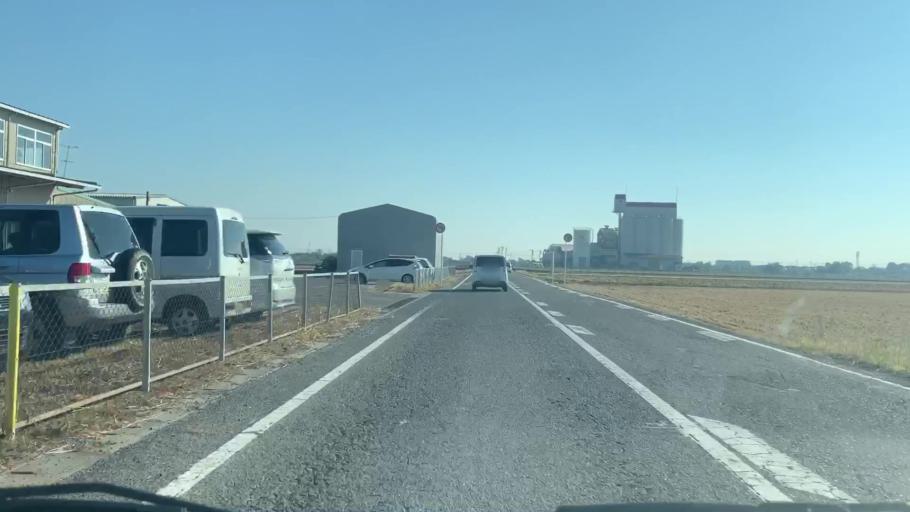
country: JP
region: Saga Prefecture
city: Saga-shi
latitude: 33.2278
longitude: 130.2845
